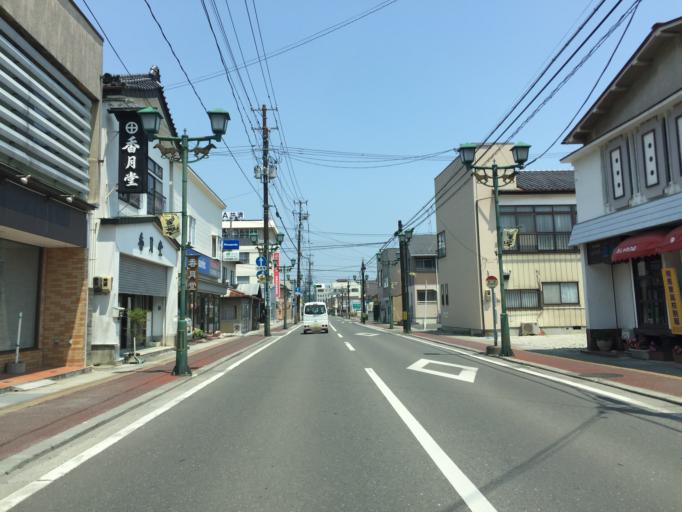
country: JP
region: Miyagi
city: Marumori
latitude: 37.7999
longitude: 140.9244
